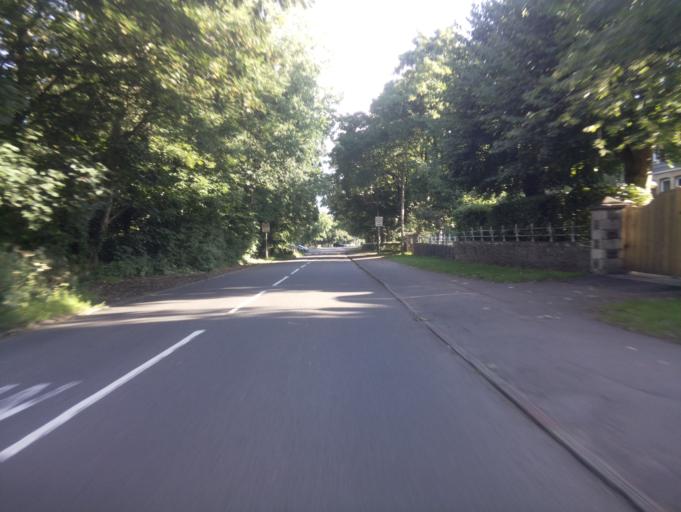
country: GB
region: England
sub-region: South Gloucestershire
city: Mangotsfield
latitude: 51.4783
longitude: -2.4842
